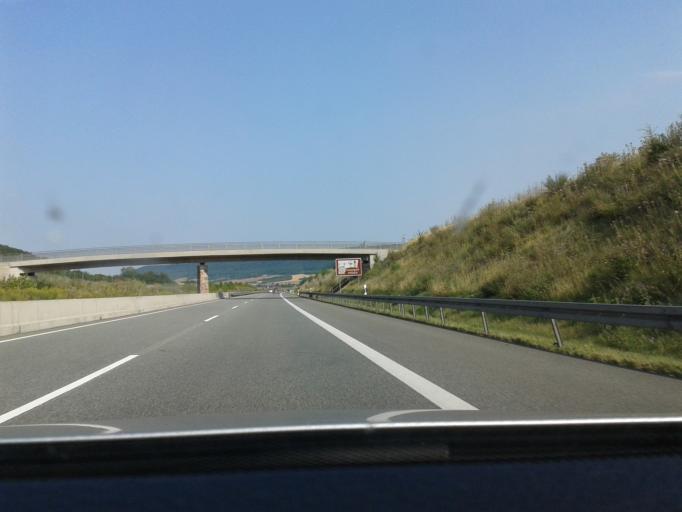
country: DE
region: Thuringia
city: Sollstedt
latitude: 51.4213
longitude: 10.5415
